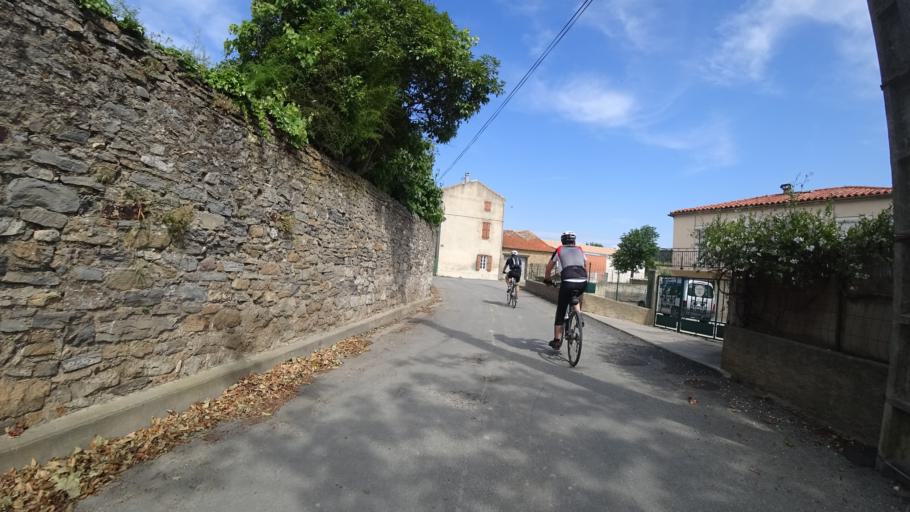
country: FR
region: Languedoc-Roussillon
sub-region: Departement de l'Aude
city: Canet
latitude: 43.2484
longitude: 2.8009
